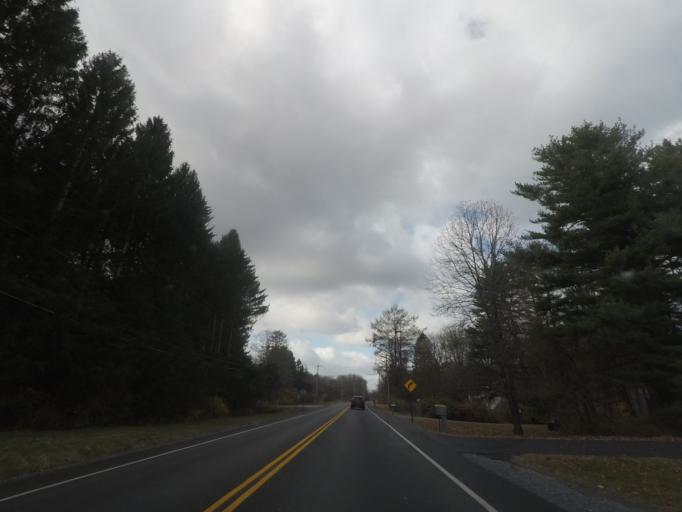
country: US
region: New York
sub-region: Saratoga County
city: Ballston Spa
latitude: 43.0118
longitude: -73.7928
